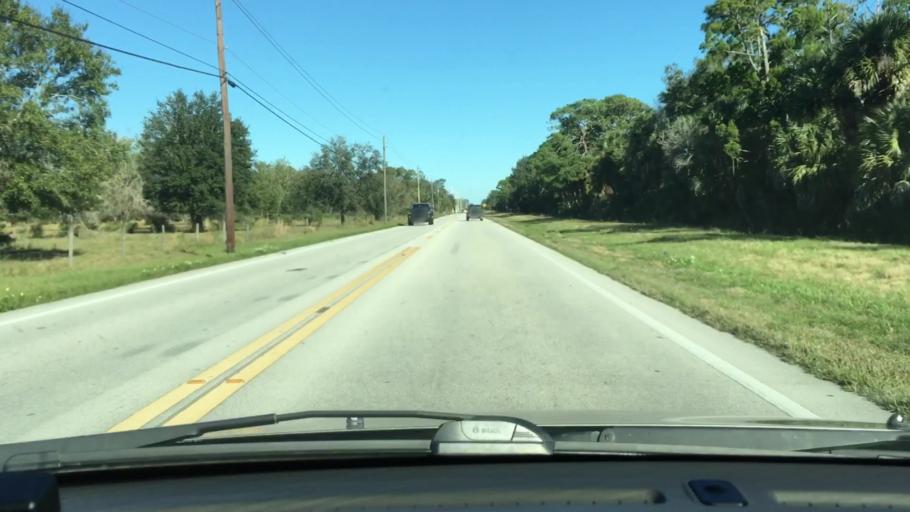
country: US
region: Florida
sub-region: Indian River County
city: Winter Beach
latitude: 27.7132
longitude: -80.4625
